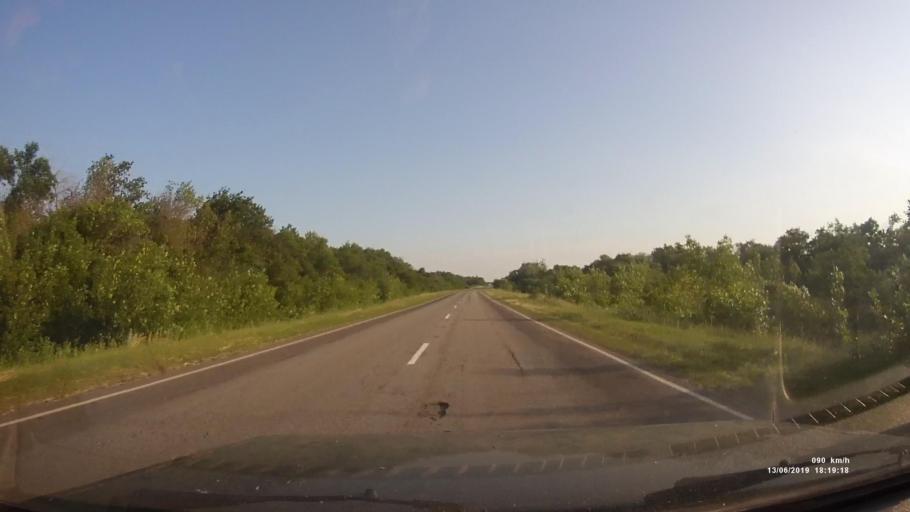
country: RU
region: Rostov
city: Kazanskaya
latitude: 49.8977
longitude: 41.3074
